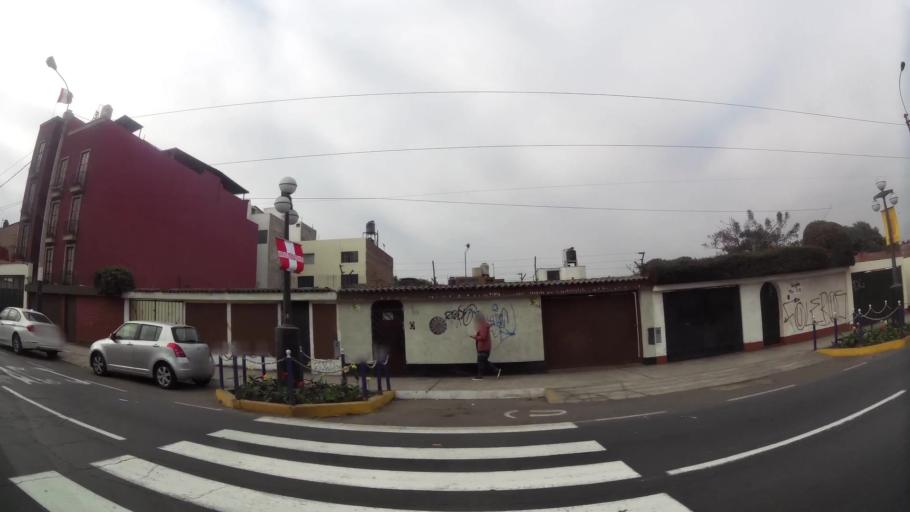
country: PE
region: Lima
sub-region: Lima
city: Surco
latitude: -12.1823
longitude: -77.0114
